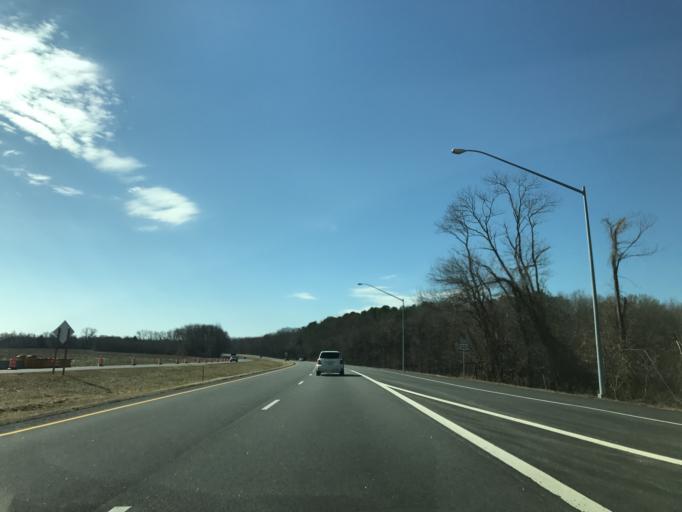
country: US
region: Maryland
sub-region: Queen Anne's County
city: Kingstown
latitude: 39.1986
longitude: -75.9038
